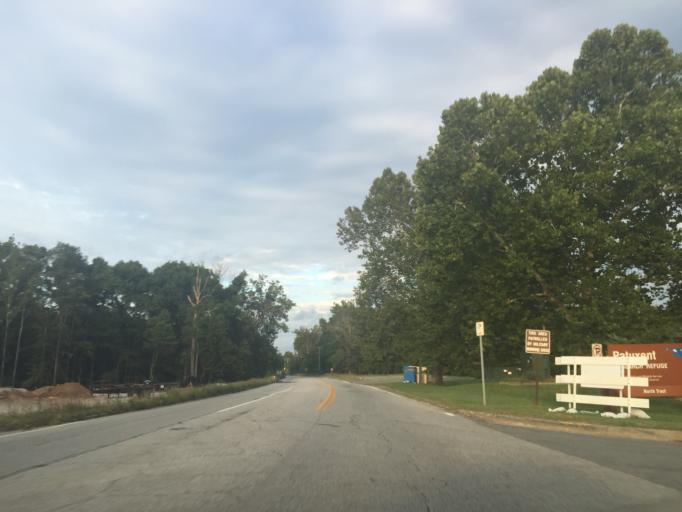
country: US
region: Maryland
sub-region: Anne Arundel County
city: Fort Meade
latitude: 39.0914
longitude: -76.7716
